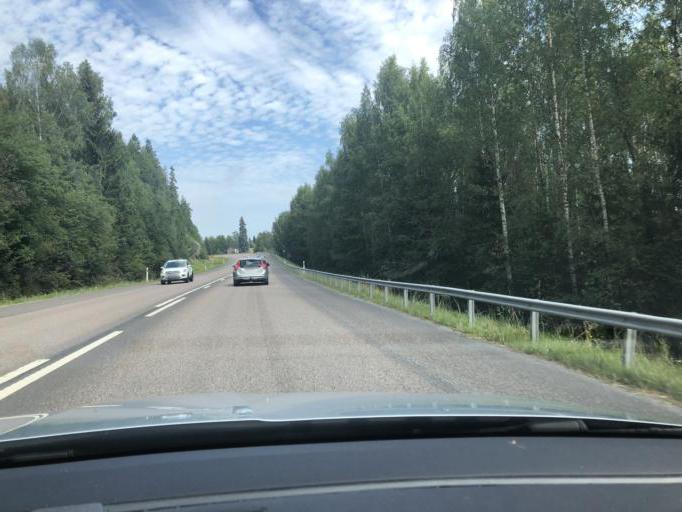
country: SE
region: Vaesternorrland
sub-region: Kramfors Kommun
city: Kramfors
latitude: 62.8841
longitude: 17.8503
